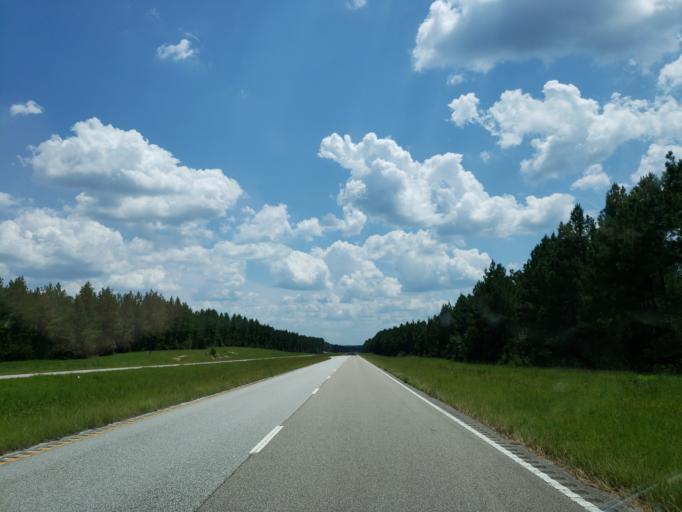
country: US
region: Mississippi
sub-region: Greene County
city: Leakesville
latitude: 31.1727
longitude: -88.5024
